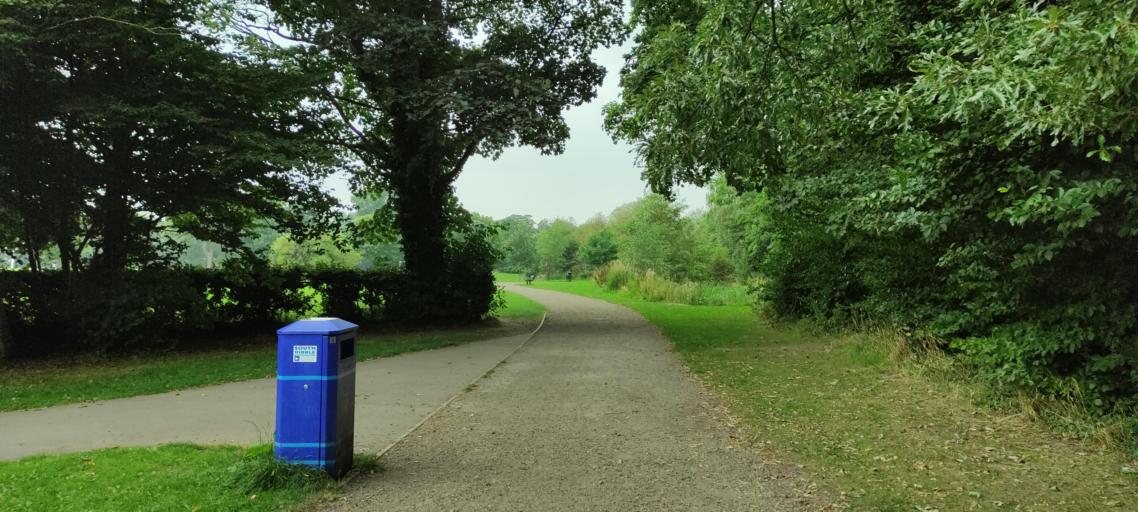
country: GB
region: England
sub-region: Lancashire
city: Leyland
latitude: 53.6864
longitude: -2.7014
